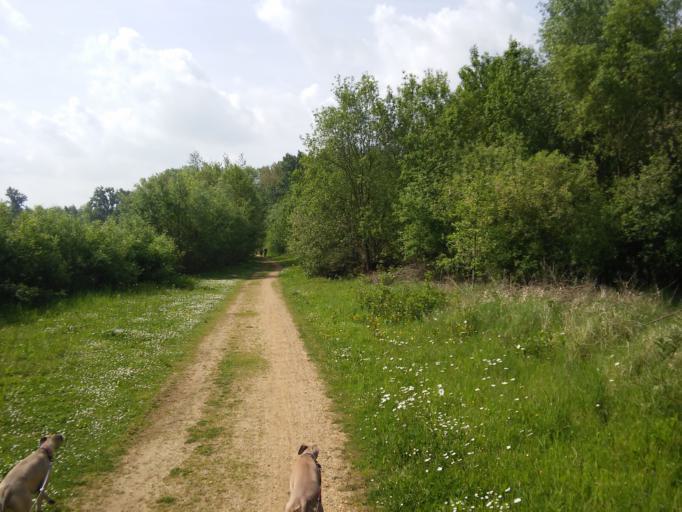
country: BE
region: Flanders
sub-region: Provincie Vlaams-Brabant
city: Zemst
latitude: 51.0081
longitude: 4.4468
